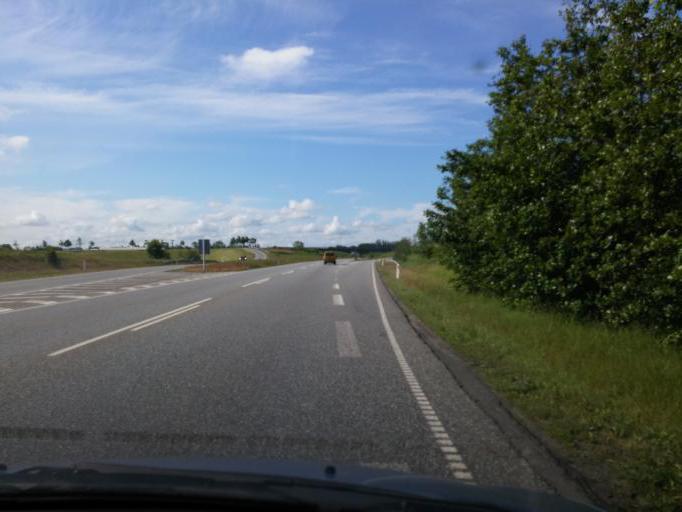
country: DK
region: South Denmark
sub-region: Odense Kommune
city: Neder Holluf
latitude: 55.3789
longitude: 10.4795
